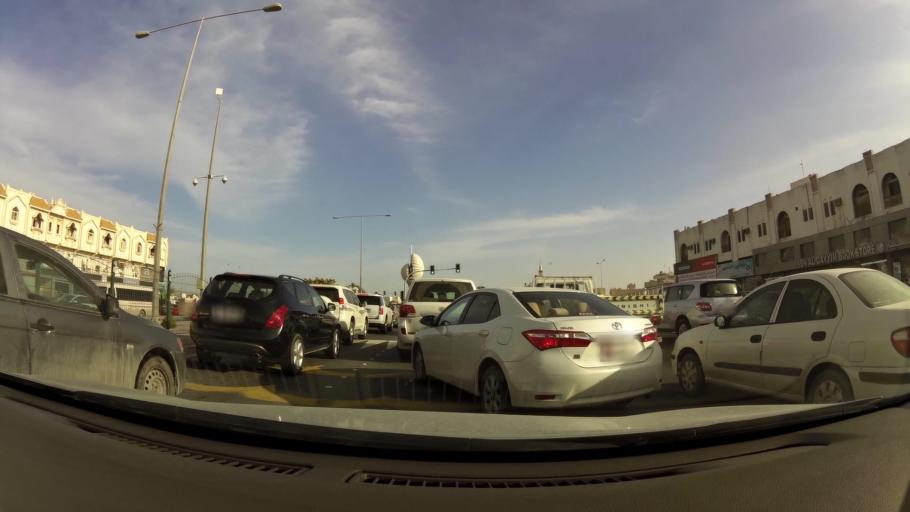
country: QA
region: Al Wakrah
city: Al Wakrah
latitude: 25.1780
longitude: 51.6042
